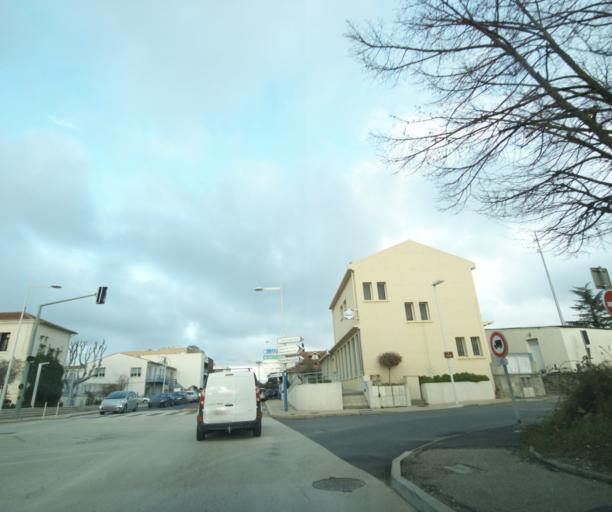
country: FR
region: Languedoc-Roussillon
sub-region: Departement de l'Herault
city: Saint-Jean-de-Vedas
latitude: 43.5753
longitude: 3.8264
